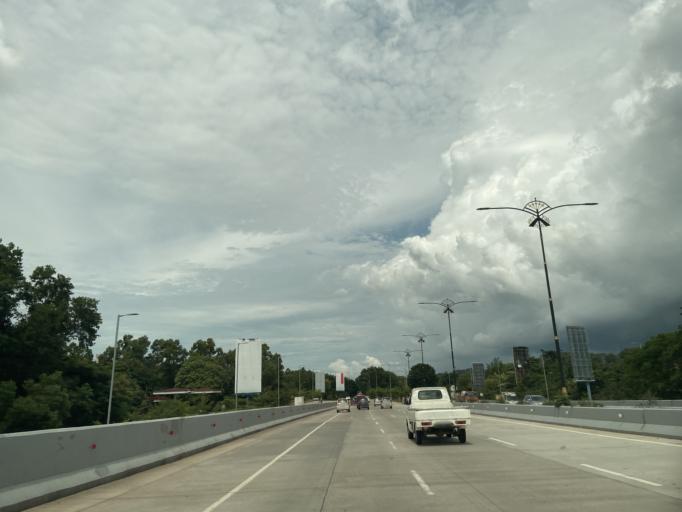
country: SG
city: Singapore
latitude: 1.1229
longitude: 104.0191
